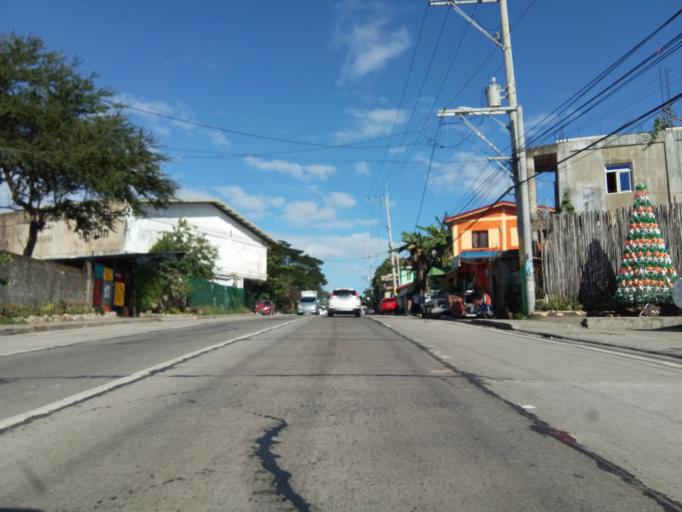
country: PH
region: Calabarzon
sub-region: Province of Cavite
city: Dasmarinas
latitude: 14.3524
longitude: 120.9781
